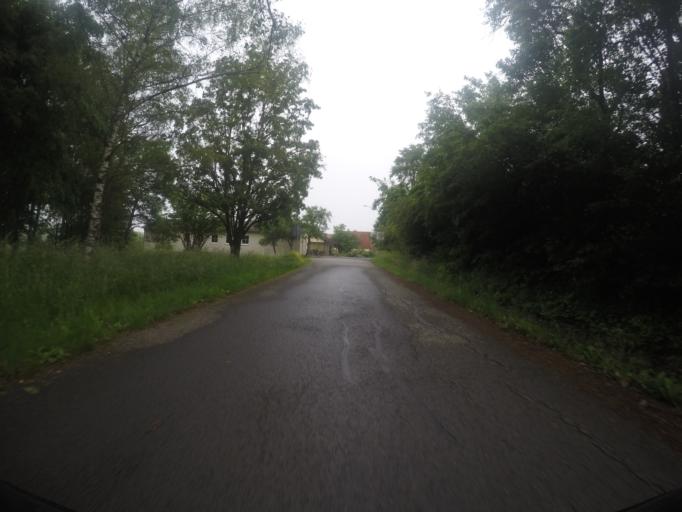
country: DE
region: Bavaria
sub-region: Regierungsbezirk Unterfranken
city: Schwanfeld
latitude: 49.9191
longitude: 10.1502
